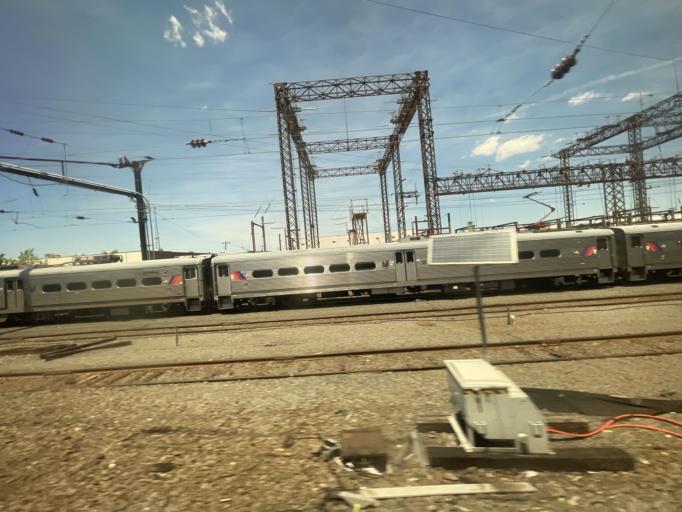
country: US
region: New Jersey
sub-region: Middlesex County
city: New Brunswick
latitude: 40.4789
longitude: -74.4655
